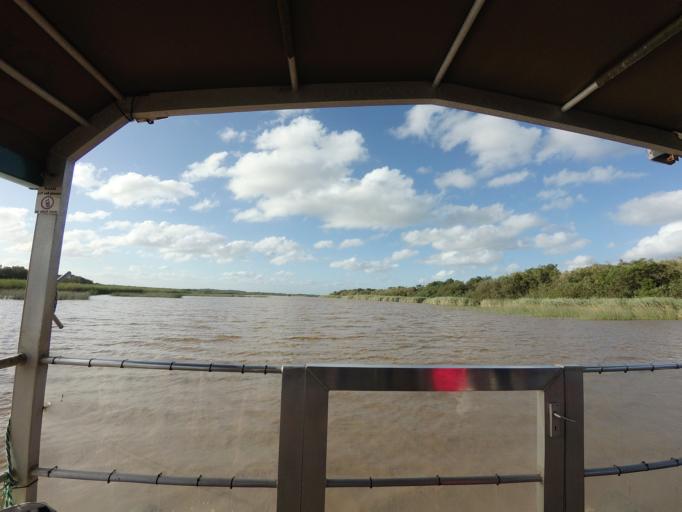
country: ZA
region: KwaZulu-Natal
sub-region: uMkhanyakude District Municipality
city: Mtubatuba
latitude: -28.3662
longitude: 32.4103
